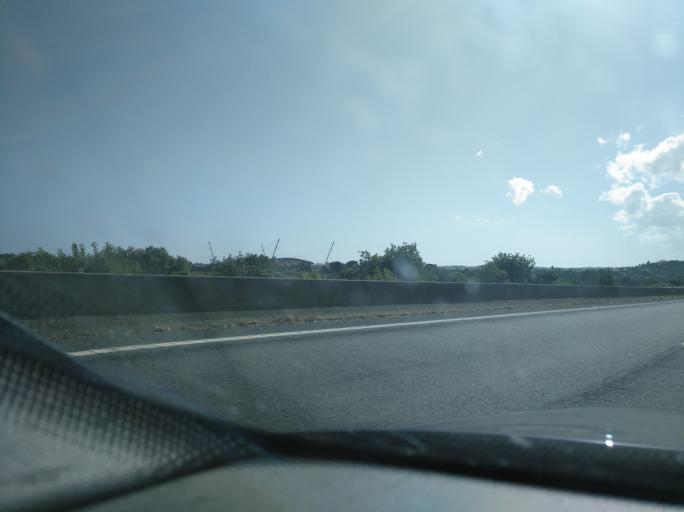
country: PT
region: Faro
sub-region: Faro
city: Santa Barbara de Nexe
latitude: 37.0945
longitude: -7.9677
